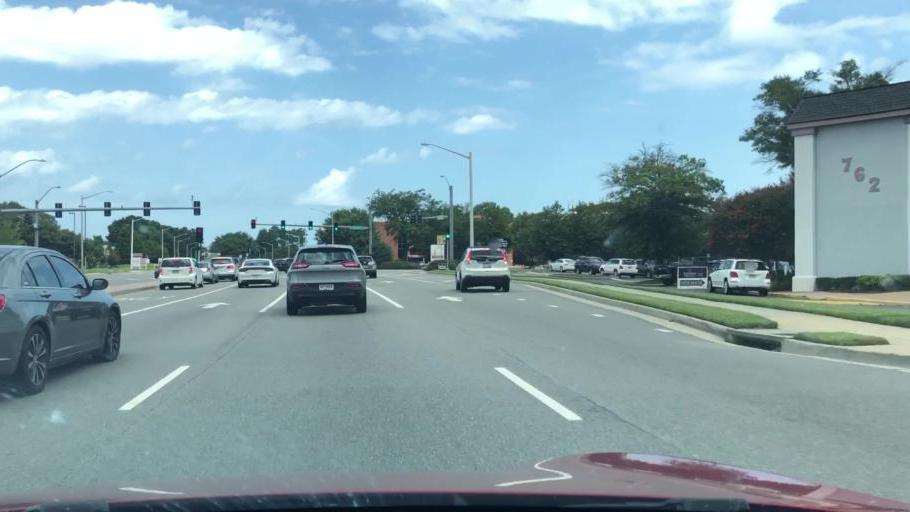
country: US
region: Virginia
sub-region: City of Chesapeake
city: Chesapeake
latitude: 36.8649
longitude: -76.1320
